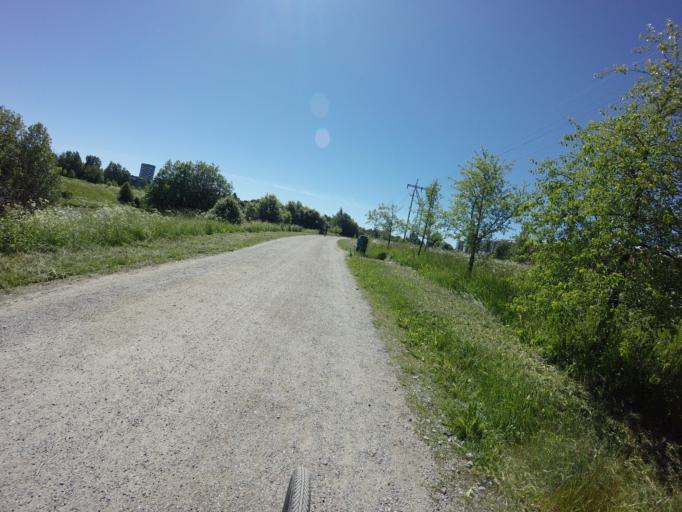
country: FI
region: Varsinais-Suomi
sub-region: Turku
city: Turku
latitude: 60.4653
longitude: 22.2847
